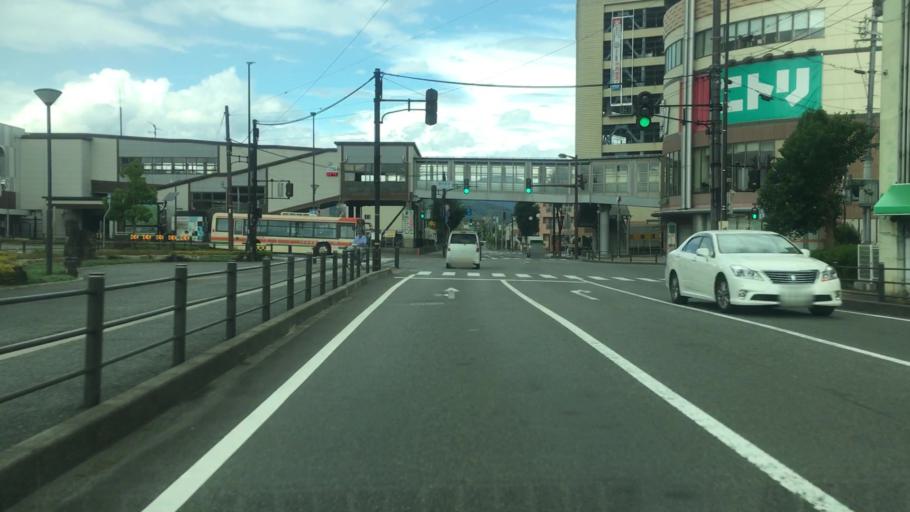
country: JP
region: Hyogo
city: Toyooka
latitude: 35.5436
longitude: 134.8146
